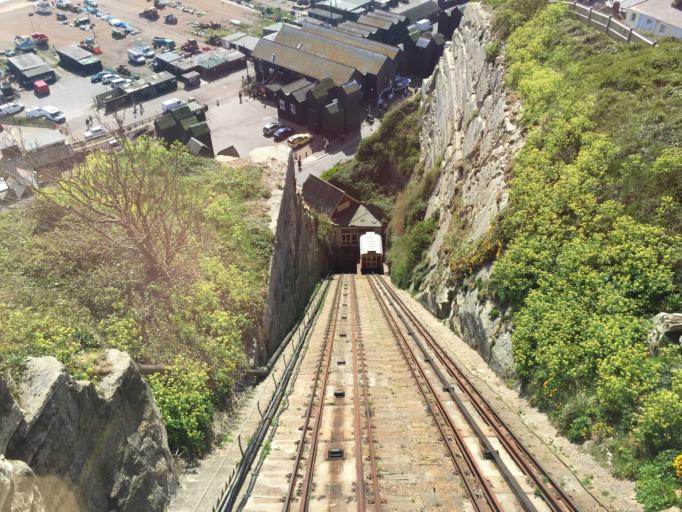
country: GB
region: England
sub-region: East Sussex
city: Hastings
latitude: 50.8568
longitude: 0.5954
